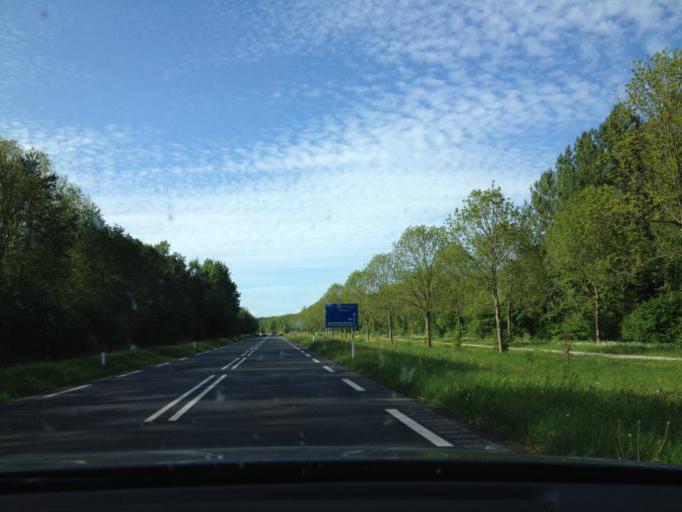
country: NL
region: Gelderland
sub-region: Gemeente Nijkerk
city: Nijkerk
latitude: 52.2683
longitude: 5.4528
